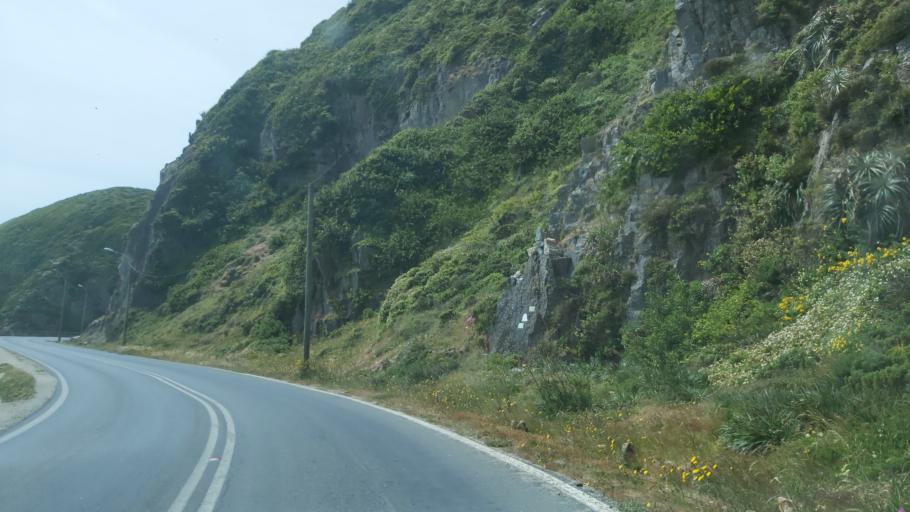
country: CL
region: Maule
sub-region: Provincia de Talca
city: Constitucion
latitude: -35.3323
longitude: -72.4337
